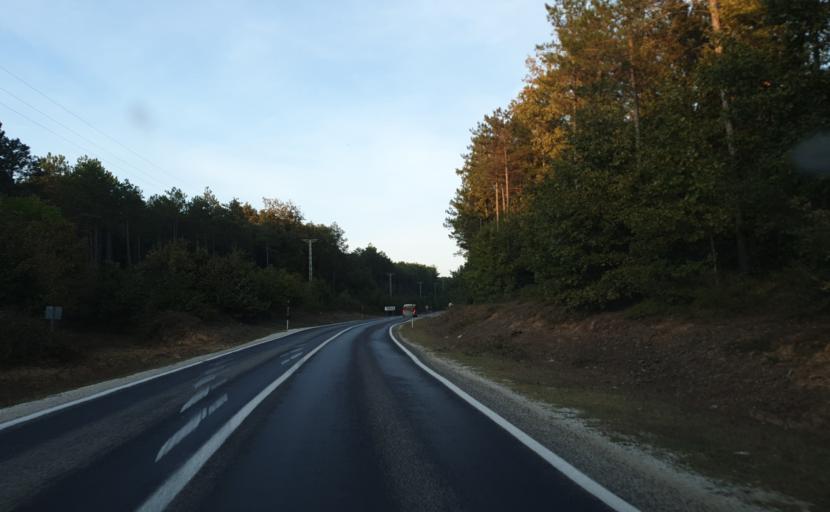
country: TR
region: Kirklareli
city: Igneada
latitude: 41.8565
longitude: 27.8092
